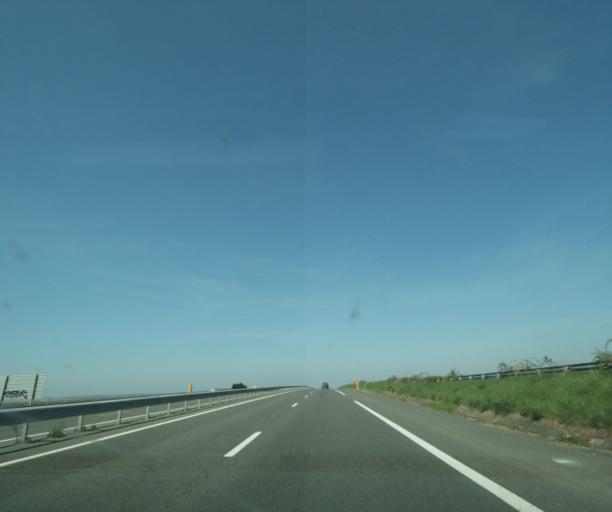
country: FR
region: Bourgogne
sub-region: Departement de la Nievre
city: Pouilly-sur-Loire
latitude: 47.3081
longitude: 2.9454
